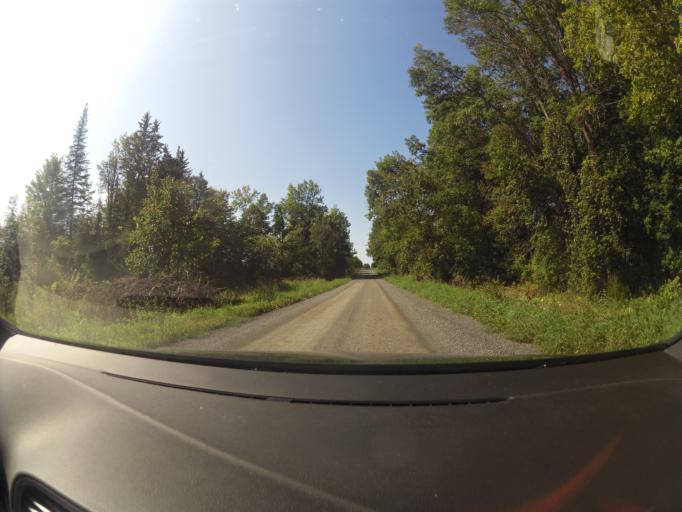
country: CA
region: Ontario
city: Arnprior
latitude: 45.3692
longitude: -76.2843
